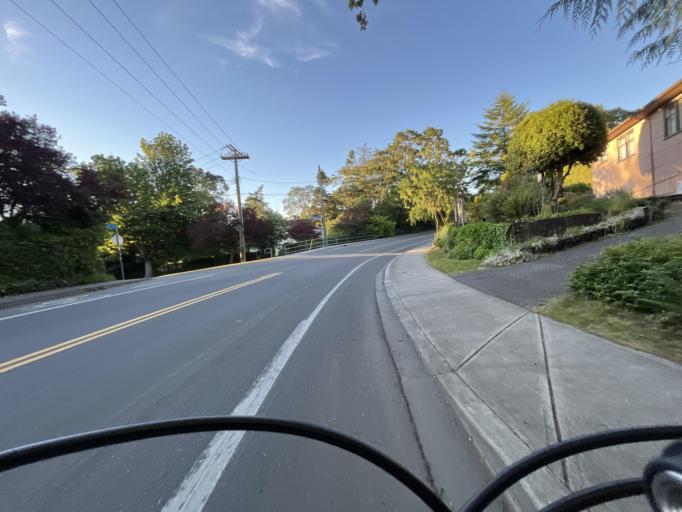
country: CA
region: British Columbia
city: Oak Bay
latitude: 48.4177
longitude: -123.3274
